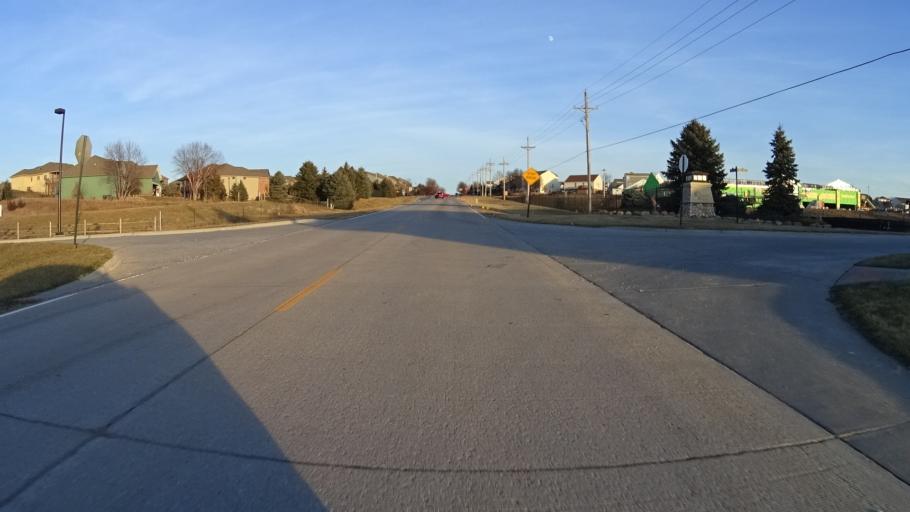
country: US
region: Nebraska
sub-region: Sarpy County
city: Papillion
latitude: 41.1326
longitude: -96.0645
